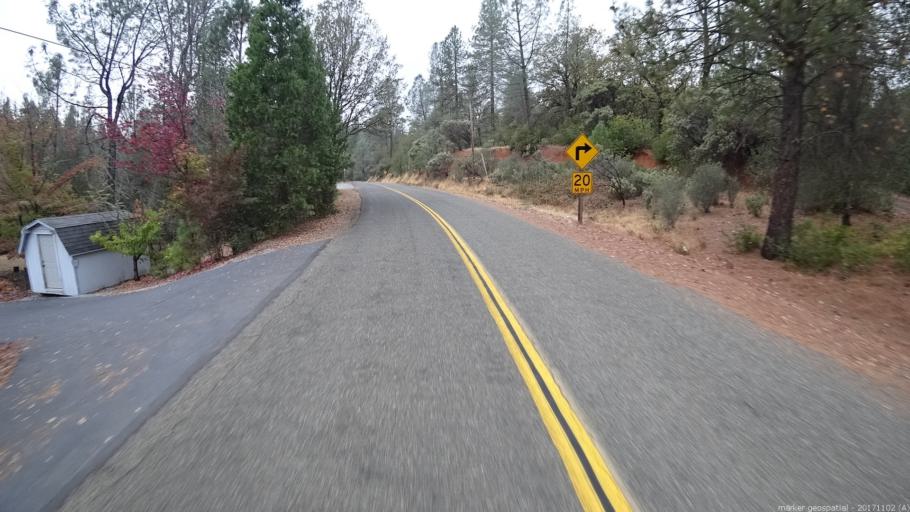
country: US
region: California
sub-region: Shasta County
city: Central Valley (historical)
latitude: 40.6638
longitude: -122.4072
